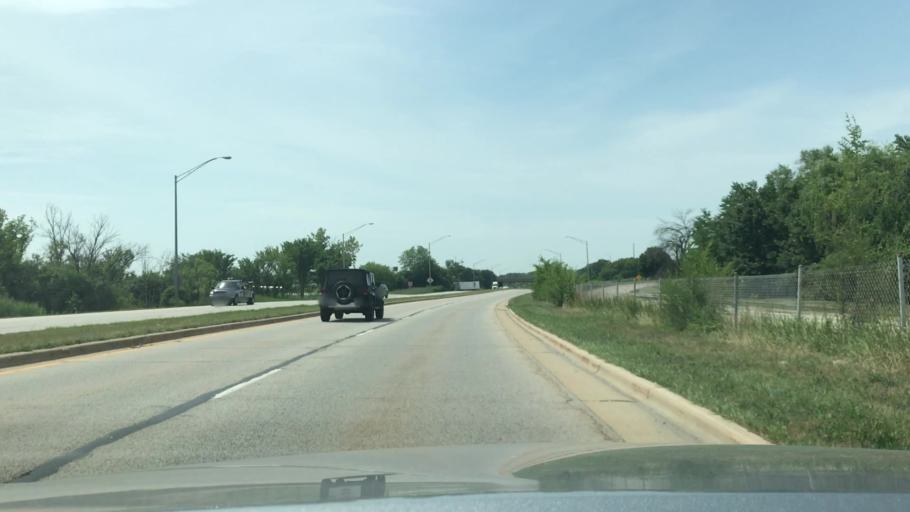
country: US
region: Illinois
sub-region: DuPage County
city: Darien
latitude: 41.7214
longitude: -88.0072
